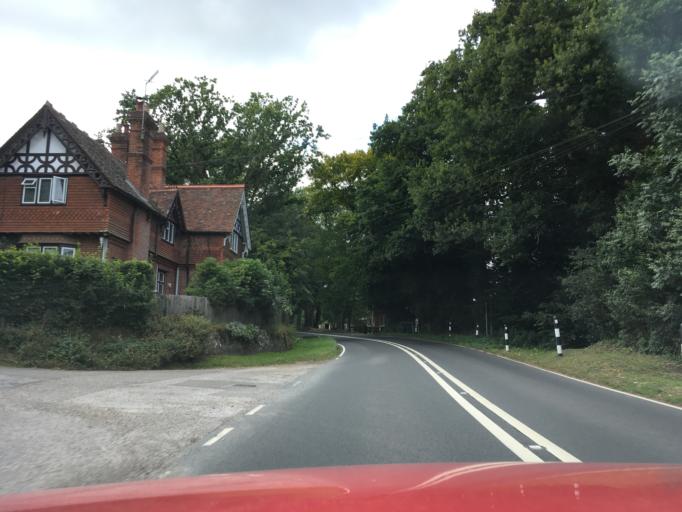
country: GB
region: England
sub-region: East Sussex
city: Forest Row
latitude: 51.1375
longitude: 0.0538
